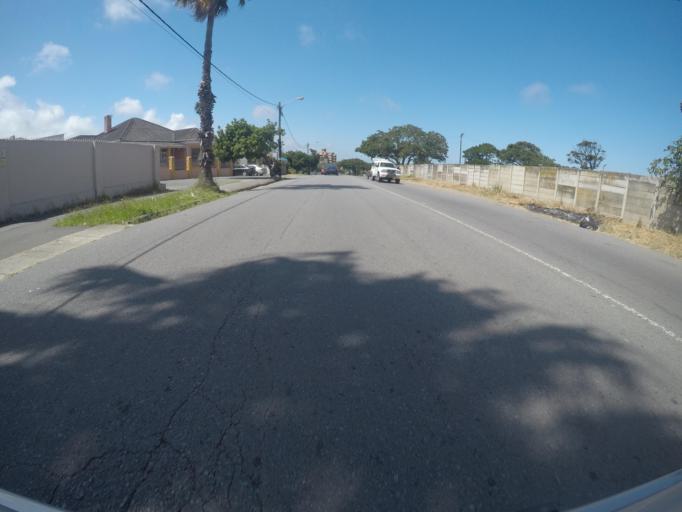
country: ZA
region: Eastern Cape
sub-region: Buffalo City Metropolitan Municipality
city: East London
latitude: -33.0051
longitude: 27.9059
